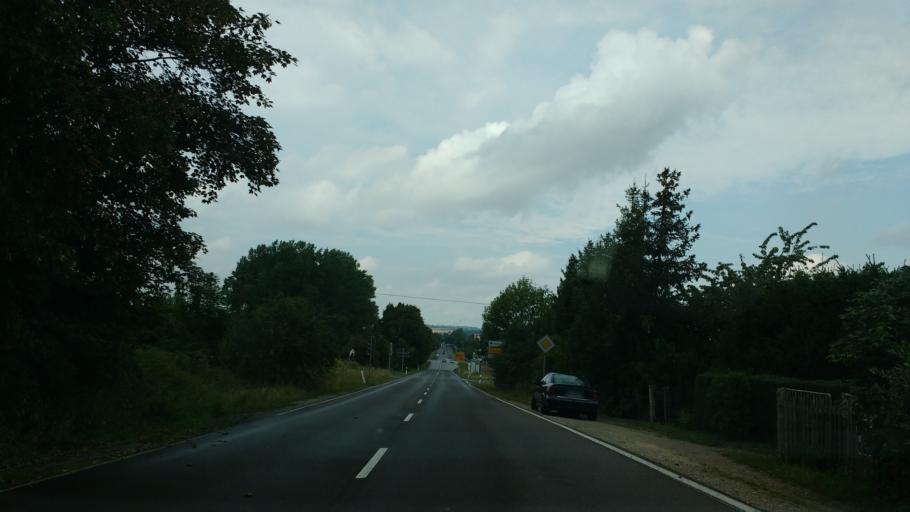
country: DE
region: Saxony-Anhalt
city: Zeitz
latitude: 51.0328
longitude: 12.1301
